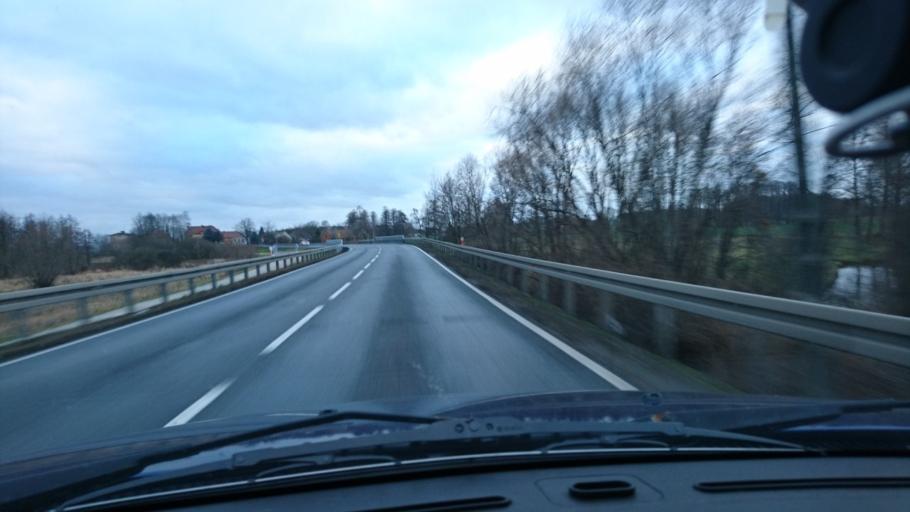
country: PL
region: Greater Poland Voivodeship
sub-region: Powiat kepinski
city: Opatow
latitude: 51.1639
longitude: 18.1526
